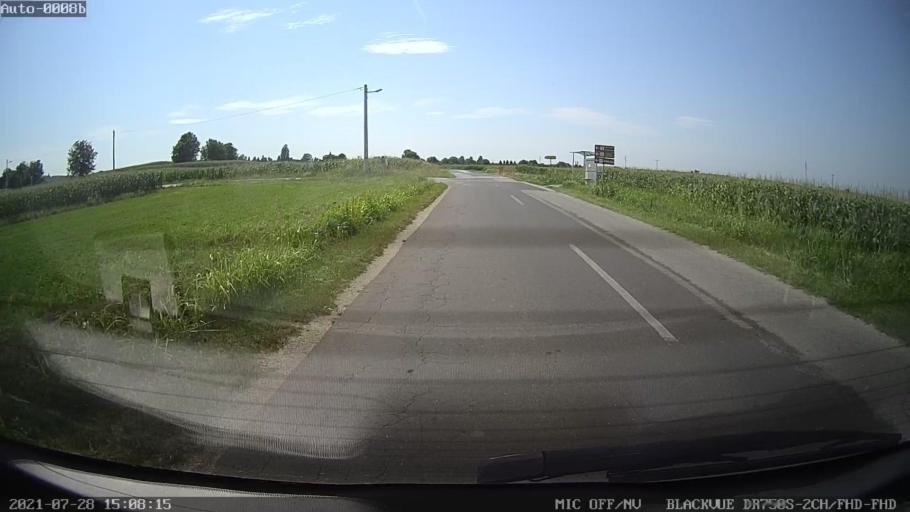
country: HR
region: Varazdinska
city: Jalzabet
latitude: 46.2587
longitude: 16.4476
